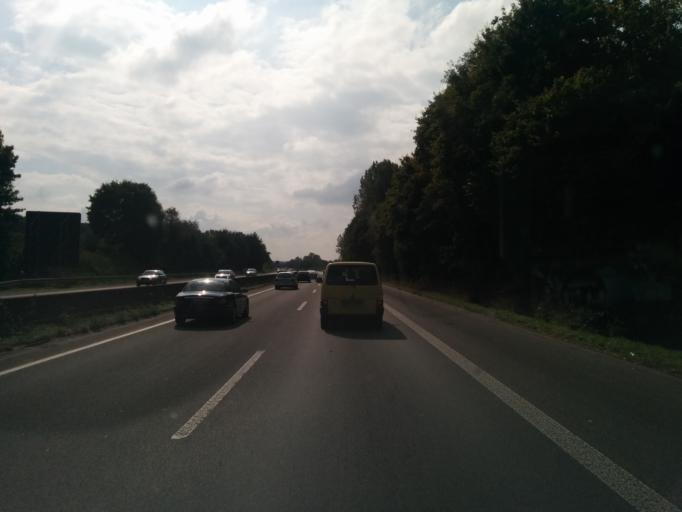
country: DE
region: North Rhine-Westphalia
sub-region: Regierungsbezirk Munster
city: Dulmen
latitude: 51.8383
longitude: 7.2461
